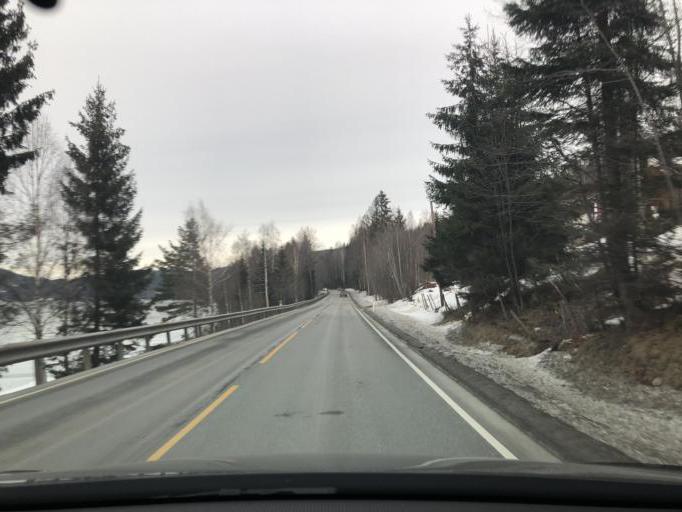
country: NO
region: Buskerud
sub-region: Ringerike
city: Honefoss
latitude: 60.4089
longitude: 10.0789
